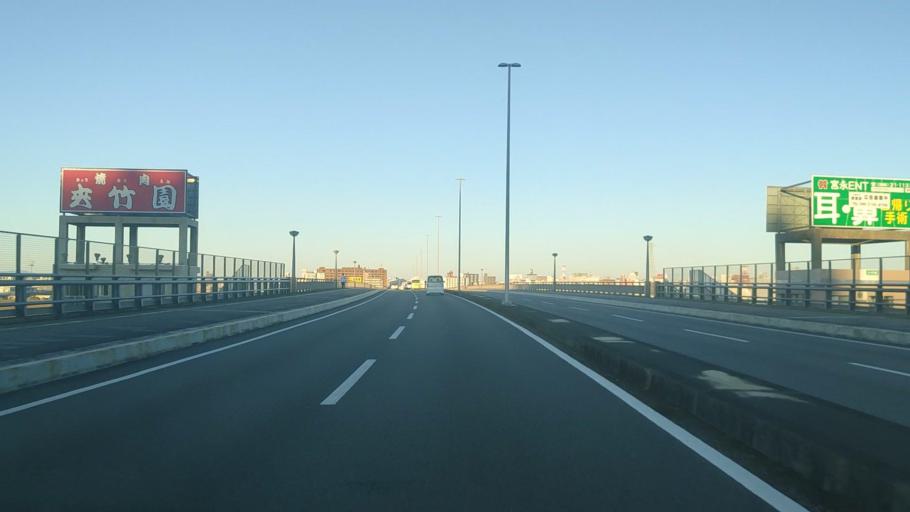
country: JP
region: Miyazaki
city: Miyazaki-shi
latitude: 31.9060
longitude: 131.4096
